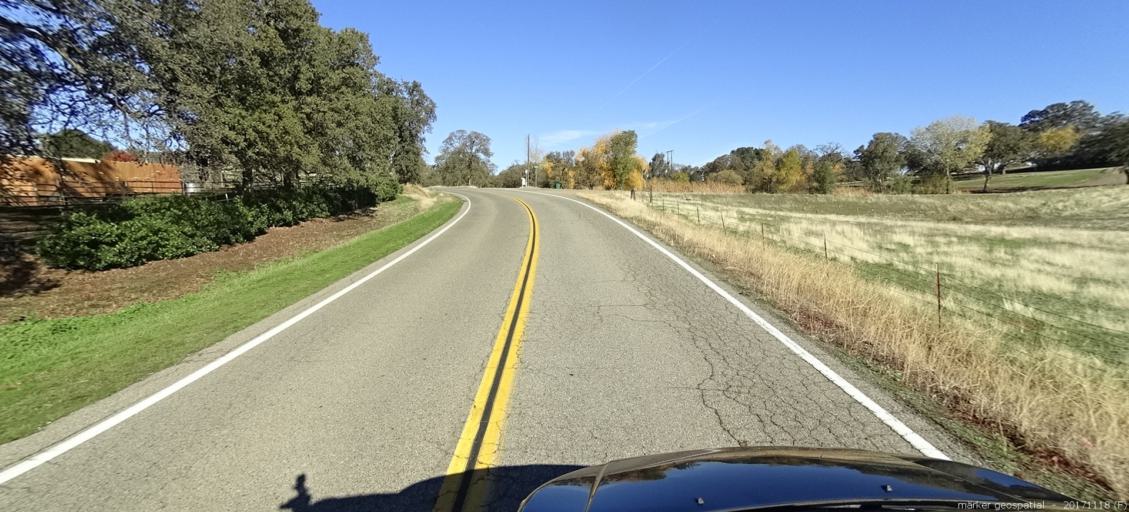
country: US
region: California
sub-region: Shasta County
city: Cottonwood
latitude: 40.3914
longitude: -122.3121
